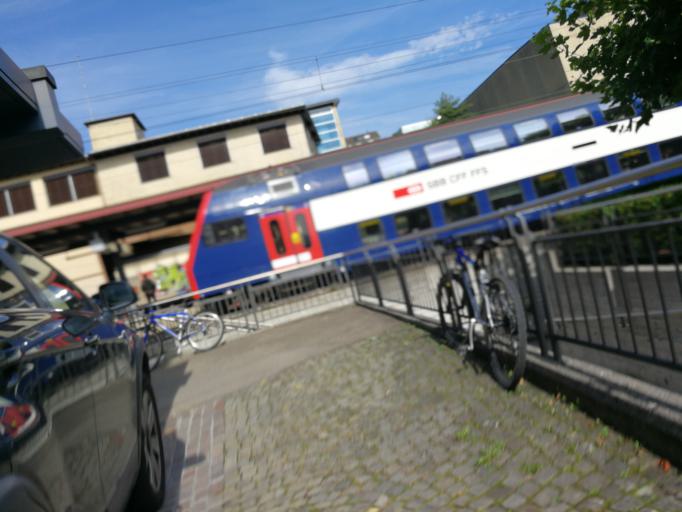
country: CH
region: Zurich
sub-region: Bezirk Meilen
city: Meilen
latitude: 47.2698
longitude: 8.6436
